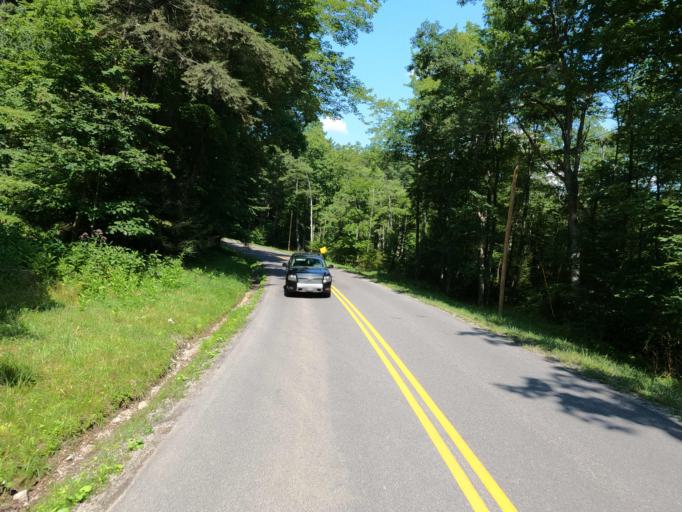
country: US
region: Maryland
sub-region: Garrett County
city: Oakland
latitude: 39.5078
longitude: -79.3994
